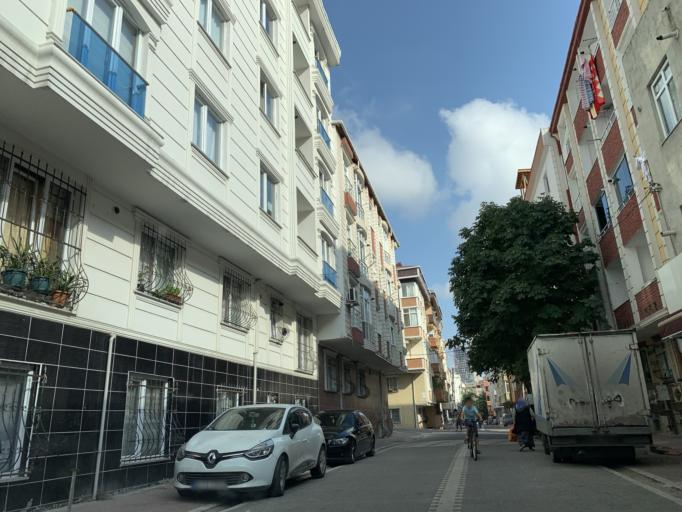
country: TR
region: Istanbul
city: Esenyurt
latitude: 41.0287
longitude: 28.6788
